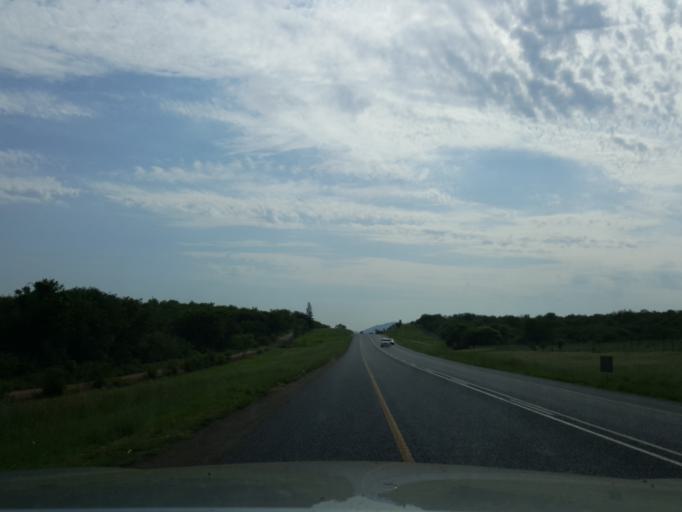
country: SZ
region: Hhohho
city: Ntfonjeni
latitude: -25.5169
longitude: 31.4414
